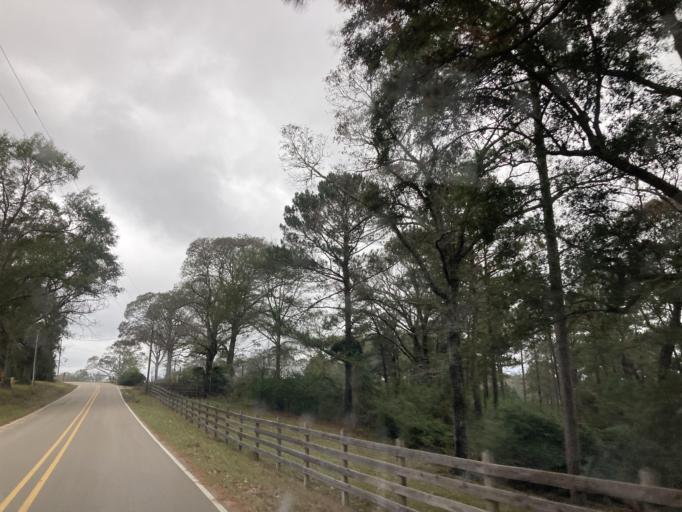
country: US
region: Mississippi
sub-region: Lamar County
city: Purvis
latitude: 31.1819
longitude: -89.4507
